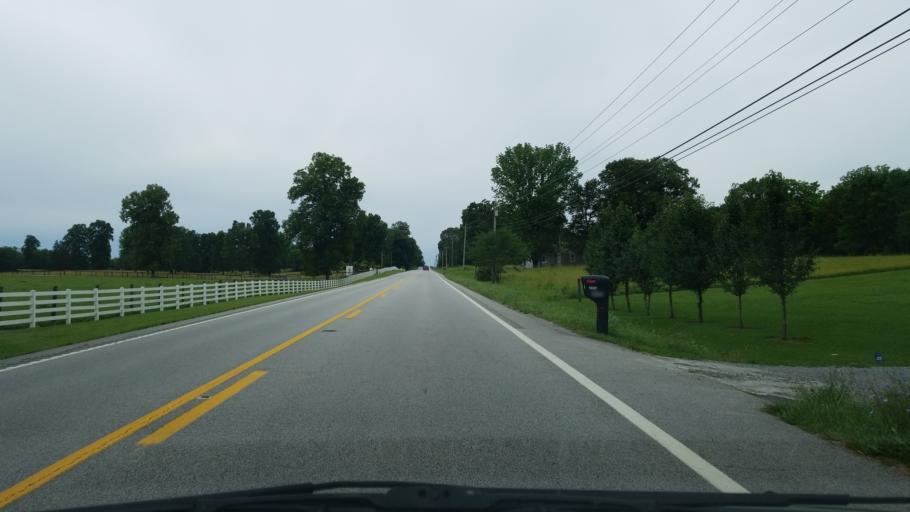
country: US
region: Tennessee
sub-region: Bradley County
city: Hopewell
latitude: 35.2859
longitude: -84.9724
